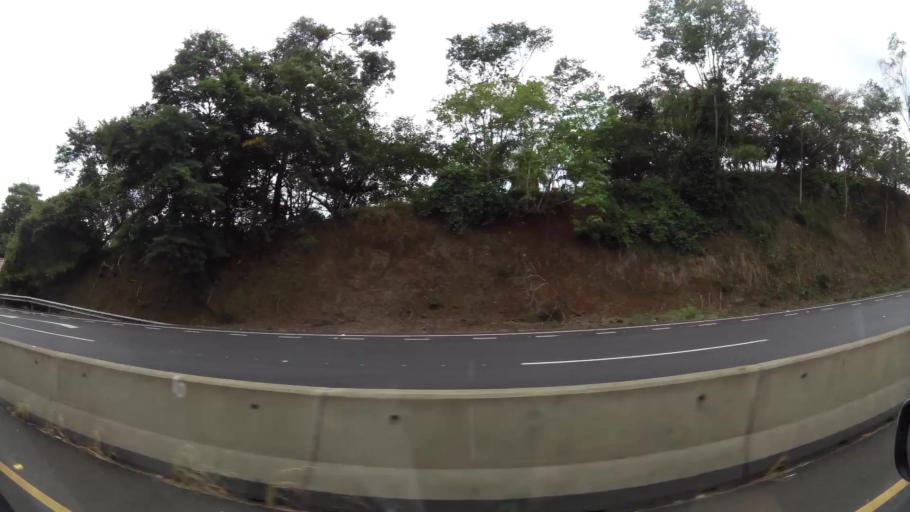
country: CR
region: Alajuela
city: Orotina
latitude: 9.8911
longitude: -84.6089
